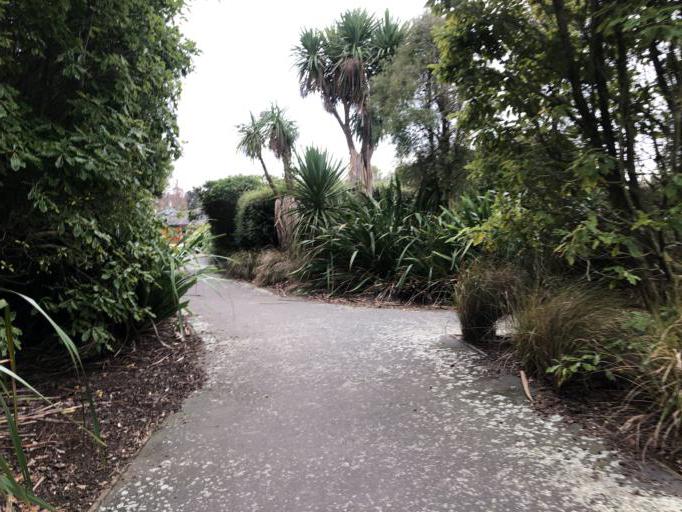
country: NZ
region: Canterbury
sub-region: Selwyn District
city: Lincoln
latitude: -43.6449
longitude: 172.4857
